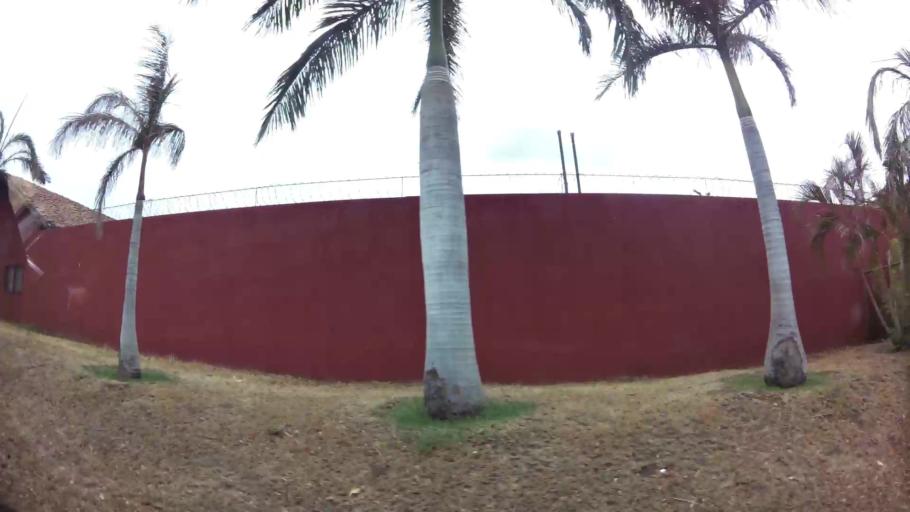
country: NI
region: Masaya
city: Ticuantepe
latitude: 12.0920
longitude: -86.1836
